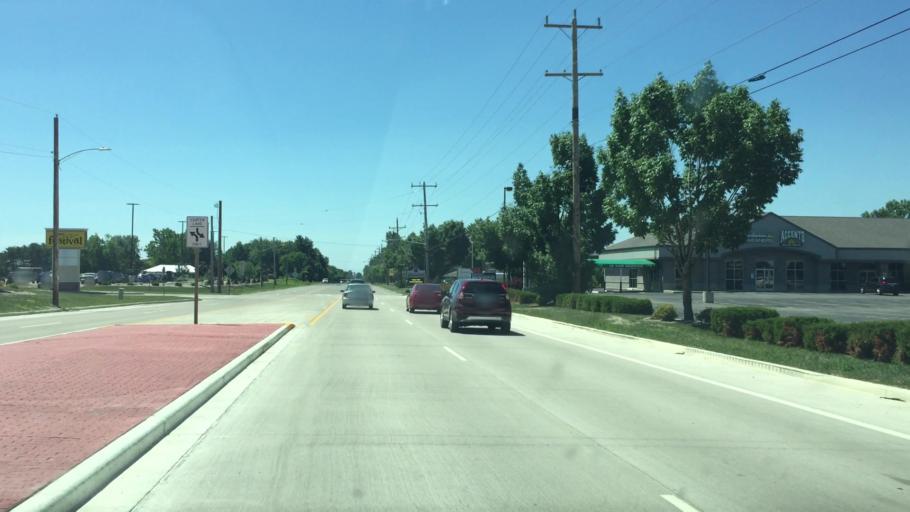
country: US
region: Wisconsin
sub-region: Outagamie County
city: Appleton
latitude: 44.2287
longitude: -88.4041
